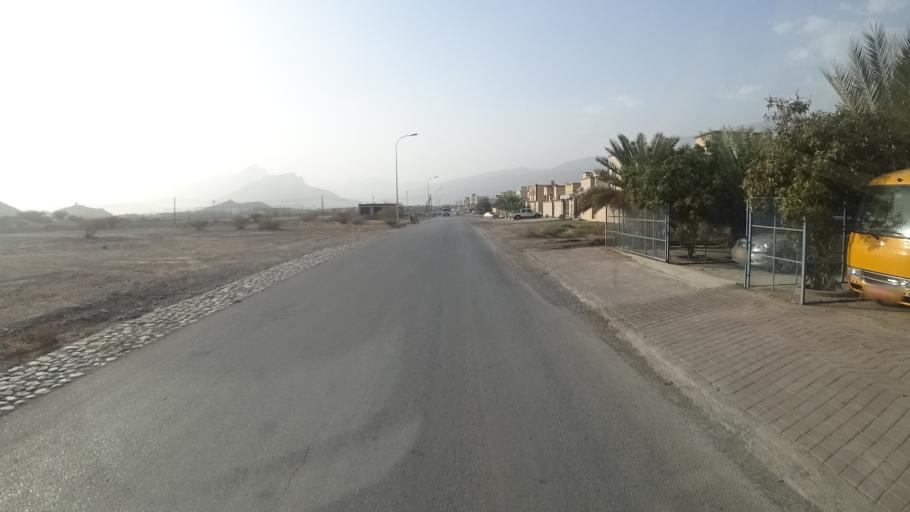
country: OM
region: Muhafazat ad Dakhiliyah
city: Bahla'
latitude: 23.0887
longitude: 57.3165
